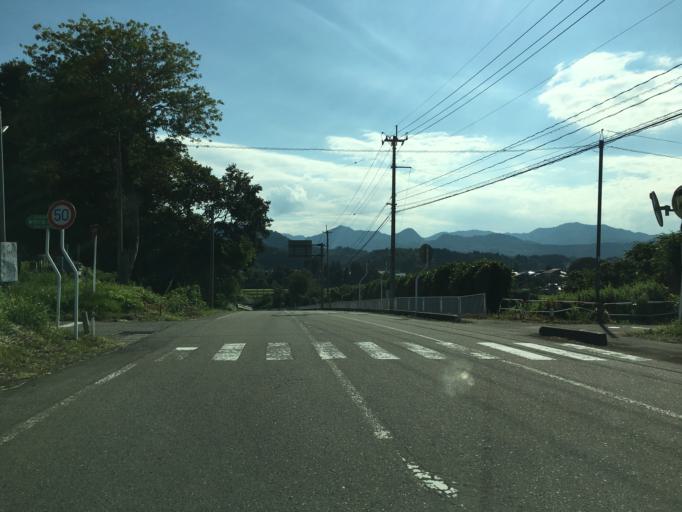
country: JP
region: Fukushima
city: Kitakata
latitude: 37.5866
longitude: 139.6572
